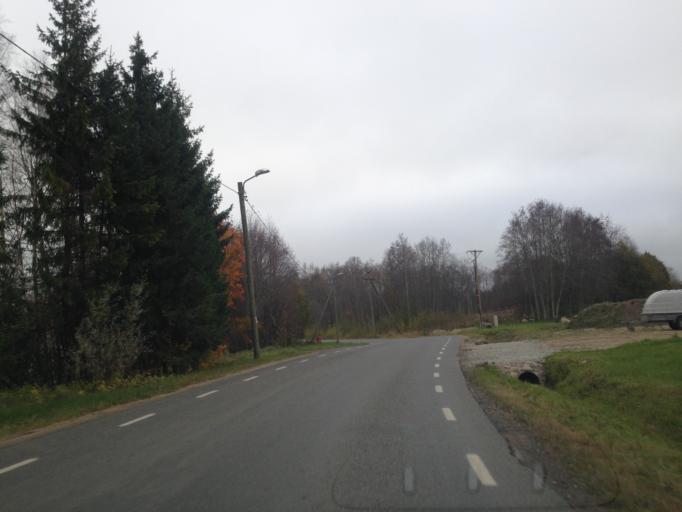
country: EE
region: Harju
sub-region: Harku vald
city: Tabasalu
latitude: 59.3776
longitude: 24.5393
